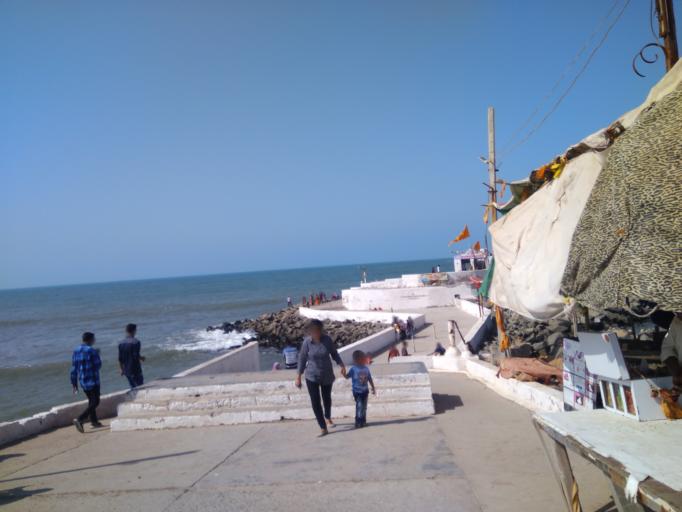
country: IN
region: Gujarat
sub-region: Jamnagar
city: Dwarka
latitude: 22.2444
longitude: 68.9549
